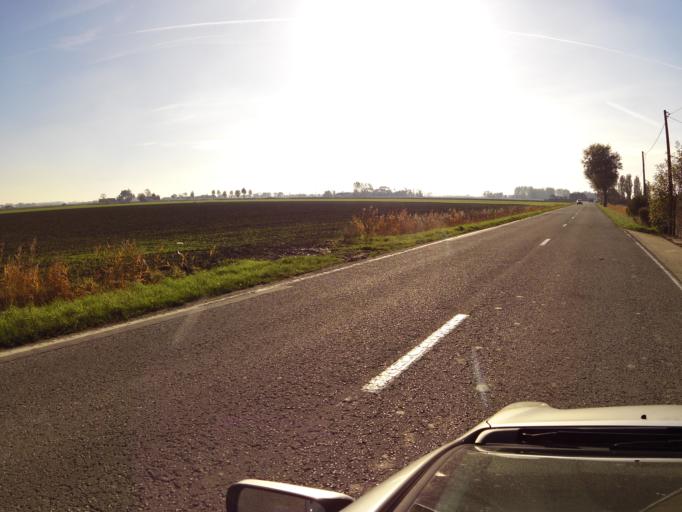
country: BE
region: Flanders
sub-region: Provincie West-Vlaanderen
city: Middelkerke
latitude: 51.1665
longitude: 2.8736
